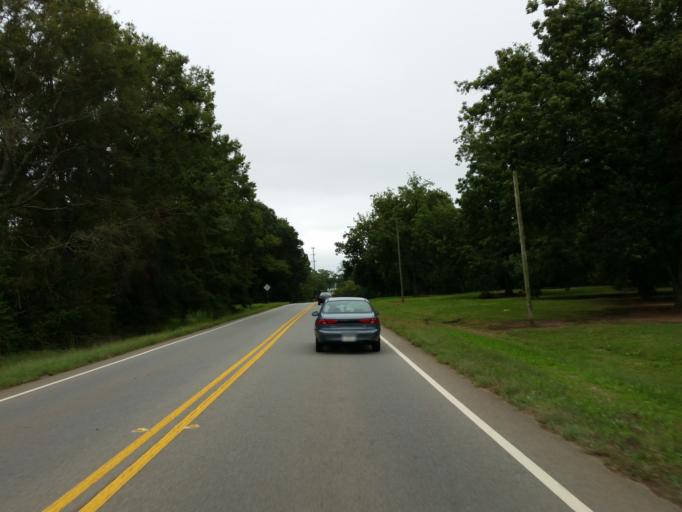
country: US
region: Georgia
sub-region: Peach County
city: Fort Valley
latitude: 32.5661
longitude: -83.8862
